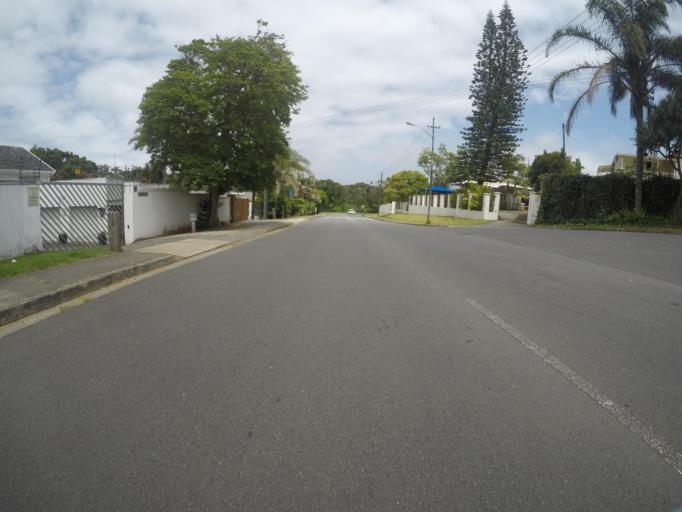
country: ZA
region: Eastern Cape
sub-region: Buffalo City Metropolitan Municipality
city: East London
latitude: -32.9908
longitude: 27.9326
